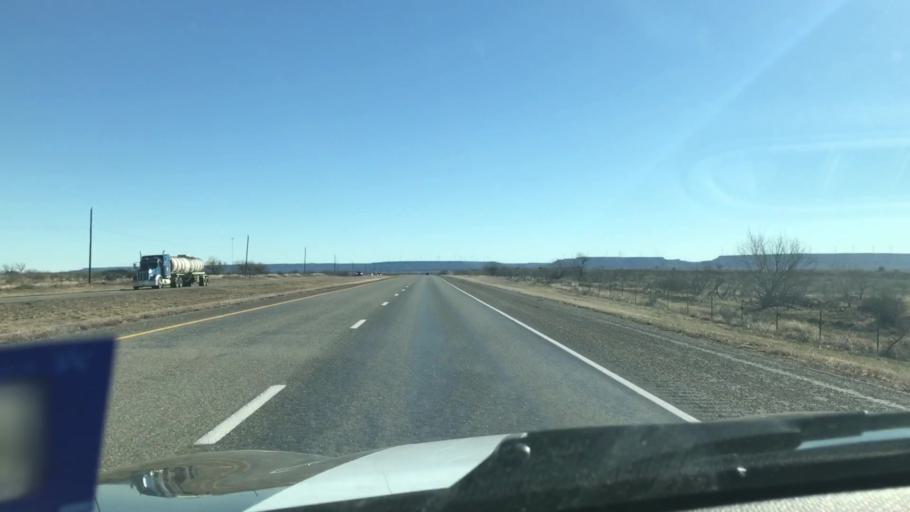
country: US
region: Texas
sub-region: Garza County
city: Post
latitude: 33.0859
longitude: -101.2426
